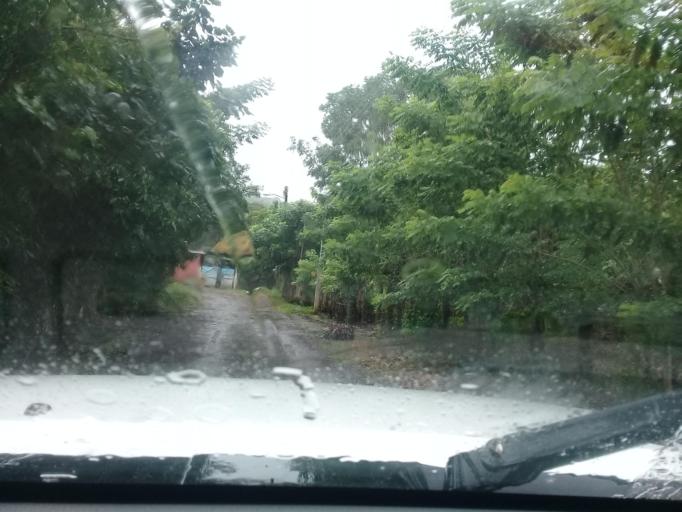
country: MX
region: Veracruz
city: Santiago Tuxtla
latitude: 18.4588
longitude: -95.3142
